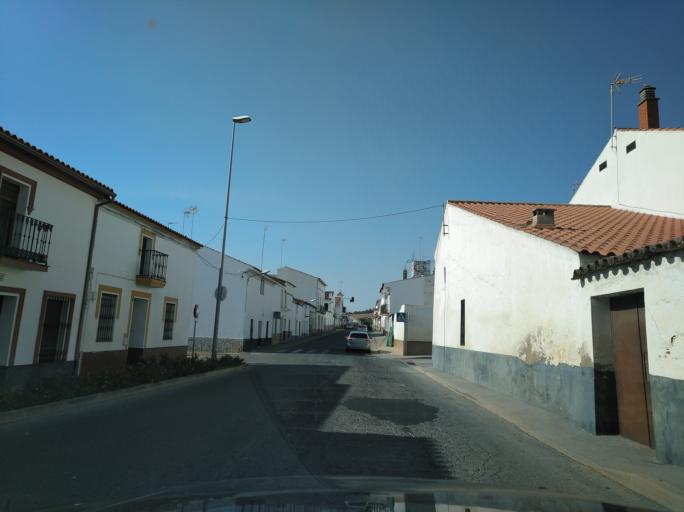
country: ES
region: Andalusia
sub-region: Provincia de Huelva
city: Rosal de la Frontera
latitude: 37.9663
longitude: -7.2222
